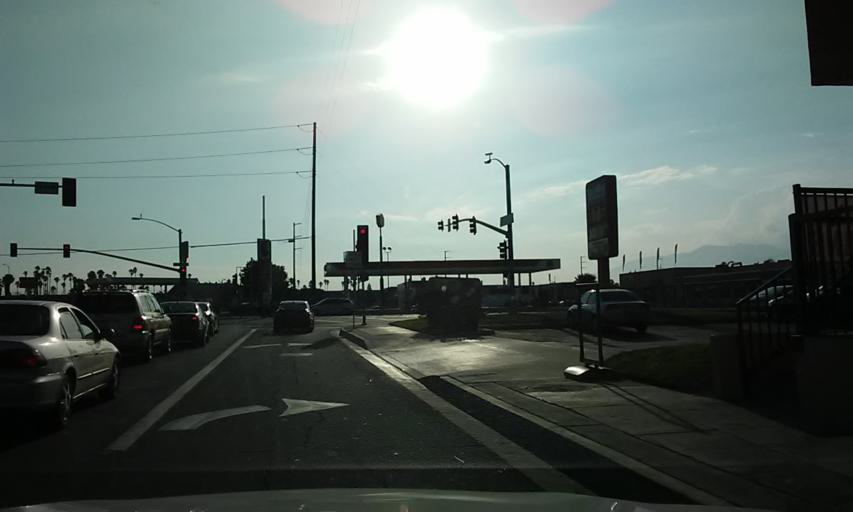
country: US
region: California
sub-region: San Bernardino County
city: Colton
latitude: 34.0797
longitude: -117.2935
